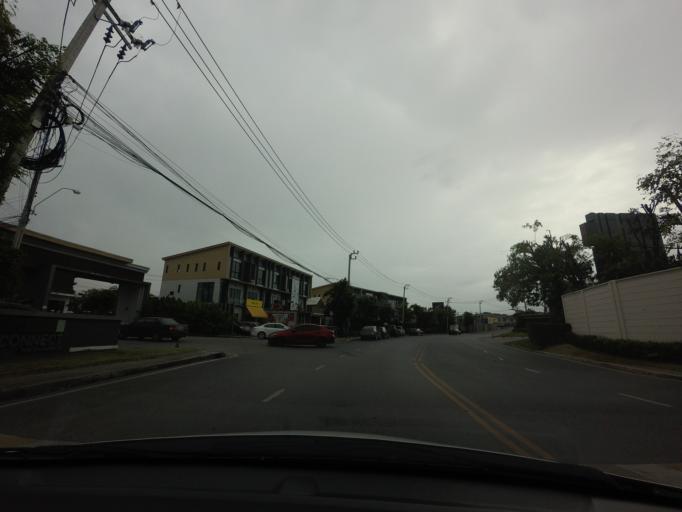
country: TH
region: Bangkok
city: Suan Luang
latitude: 13.7263
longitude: 100.6338
